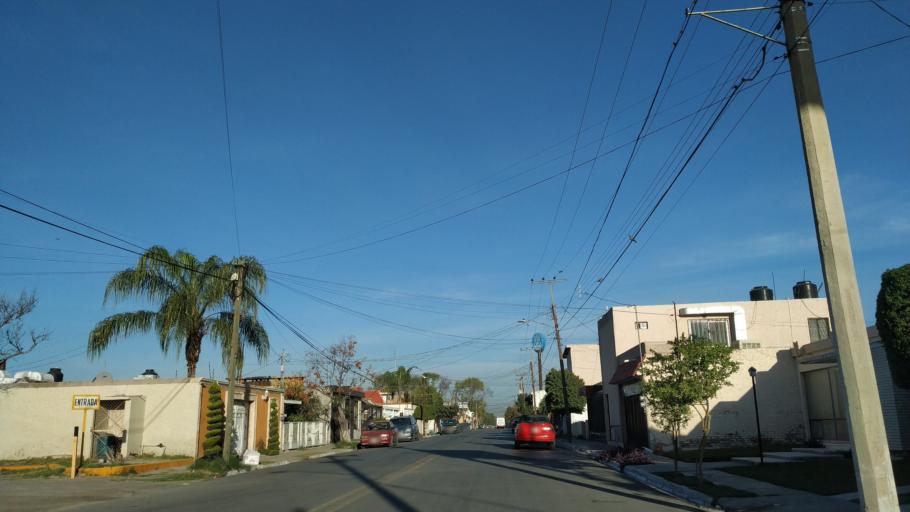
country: MX
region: Coahuila
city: Torreon
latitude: 25.5510
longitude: -103.4488
